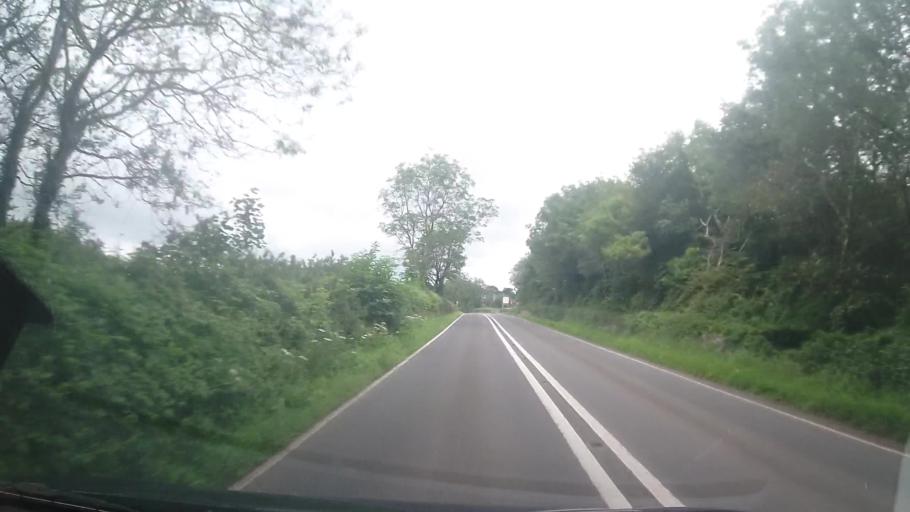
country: GB
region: Wales
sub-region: Anglesey
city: Gaerwen
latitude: 53.1859
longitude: -4.2579
